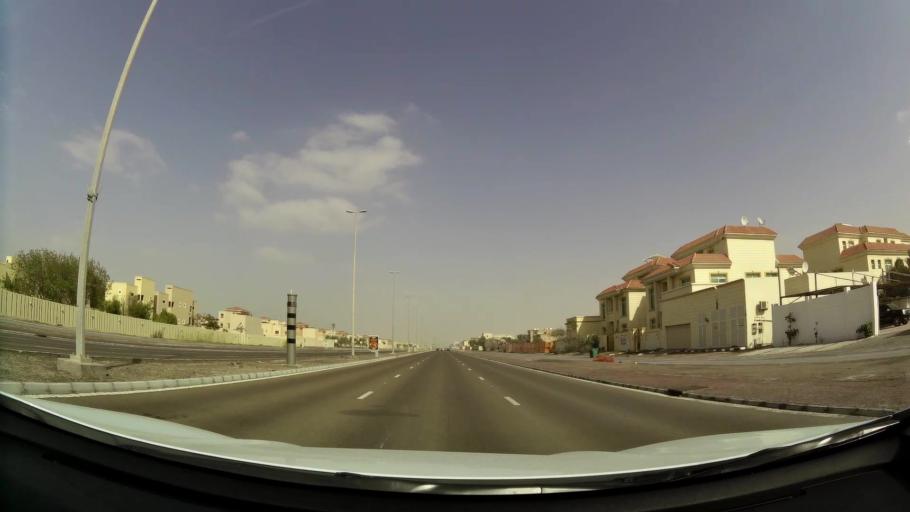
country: AE
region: Abu Dhabi
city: Abu Dhabi
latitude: 24.4272
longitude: 54.5552
